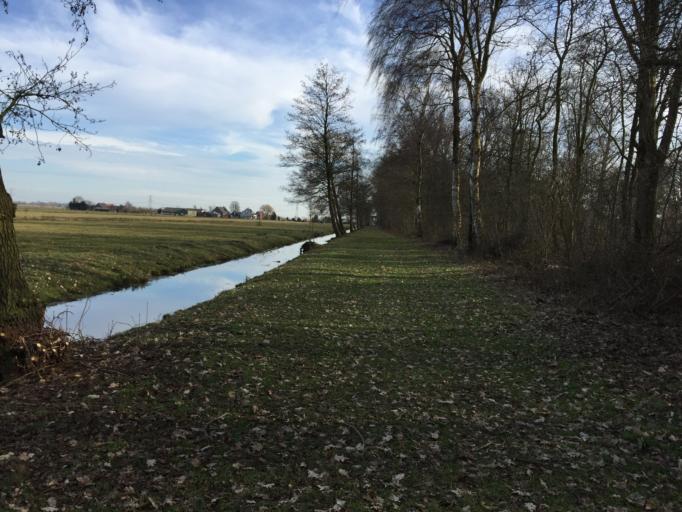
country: NL
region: South Holland
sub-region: Gemeente Vlist
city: Haastrecht
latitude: 52.0247
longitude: 4.7695
